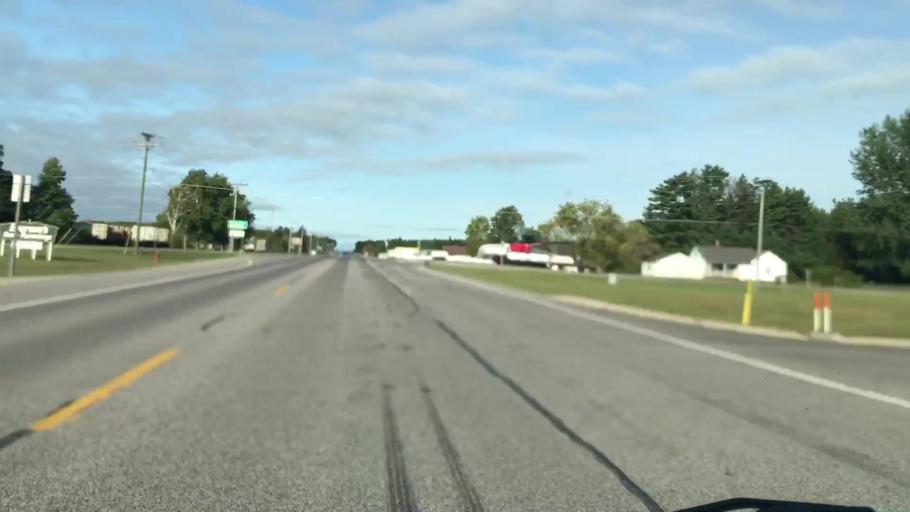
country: US
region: Michigan
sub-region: Luce County
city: Newberry
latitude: 46.3035
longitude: -85.4876
